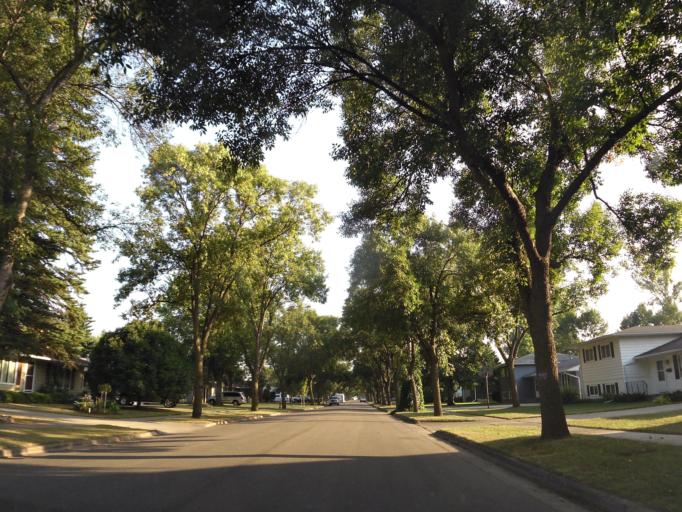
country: US
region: North Dakota
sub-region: Grand Forks County
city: Grand Forks
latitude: 47.8954
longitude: -97.0406
